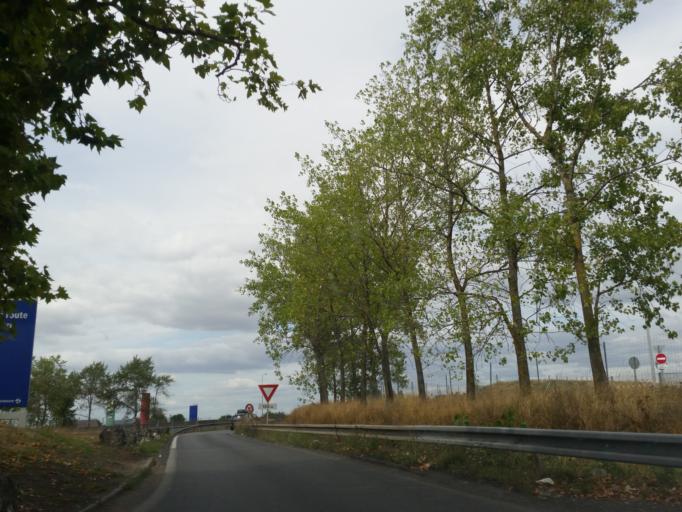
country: FR
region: Centre
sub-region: Departement d'Indre-et-Loire
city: Monnaie
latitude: 47.4744
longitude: 0.7776
